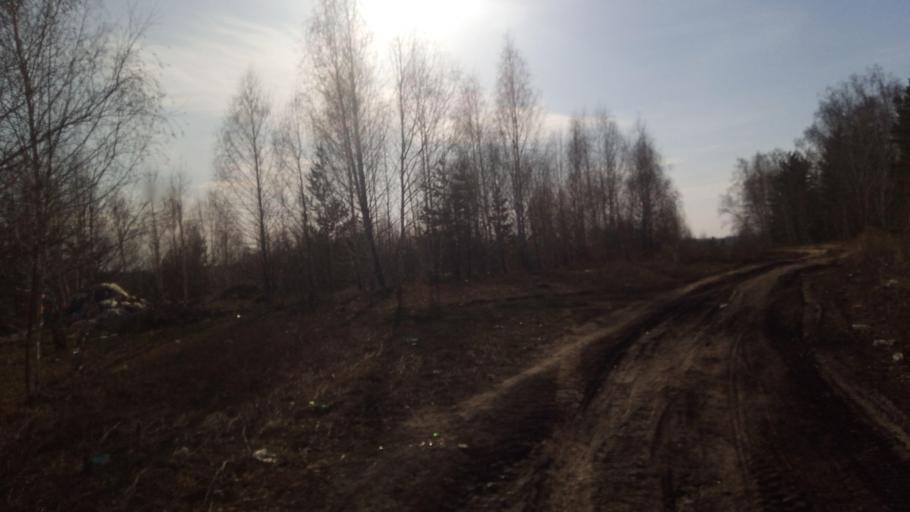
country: RU
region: Chelyabinsk
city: Sargazy
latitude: 55.1193
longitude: 61.2522
